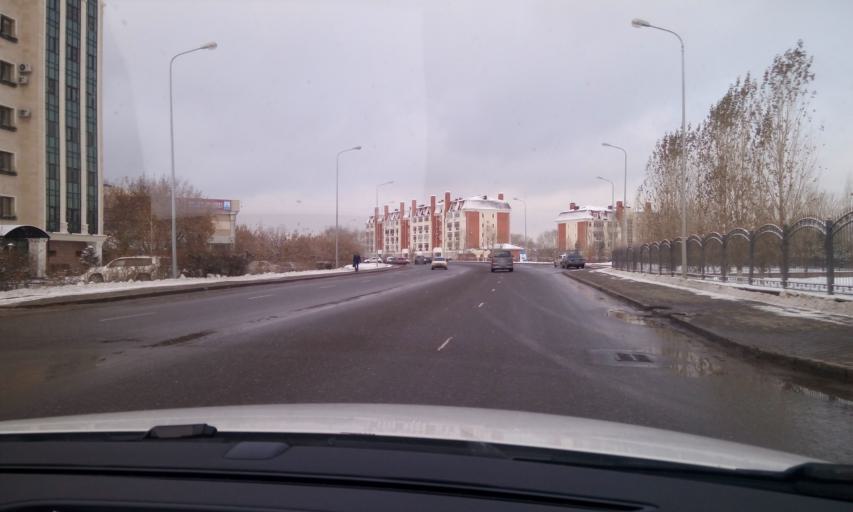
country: KZ
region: Astana Qalasy
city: Astana
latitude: 51.1348
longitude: 71.4352
